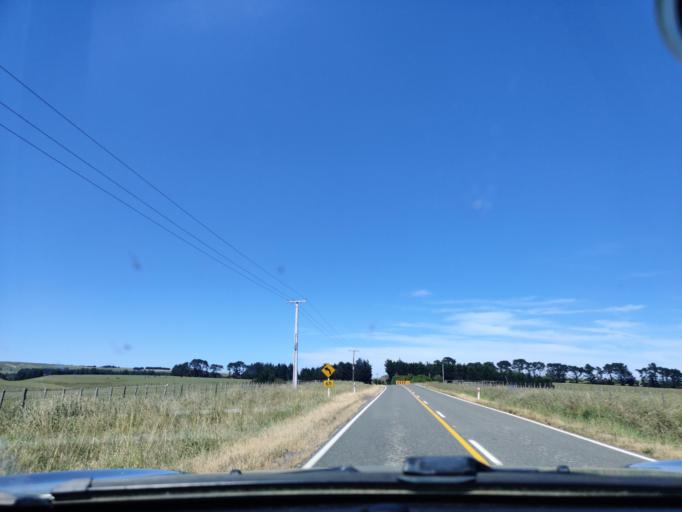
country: NZ
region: Wellington
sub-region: Upper Hutt City
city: Upper Hutt
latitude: -41.3597
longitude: 175.2005
